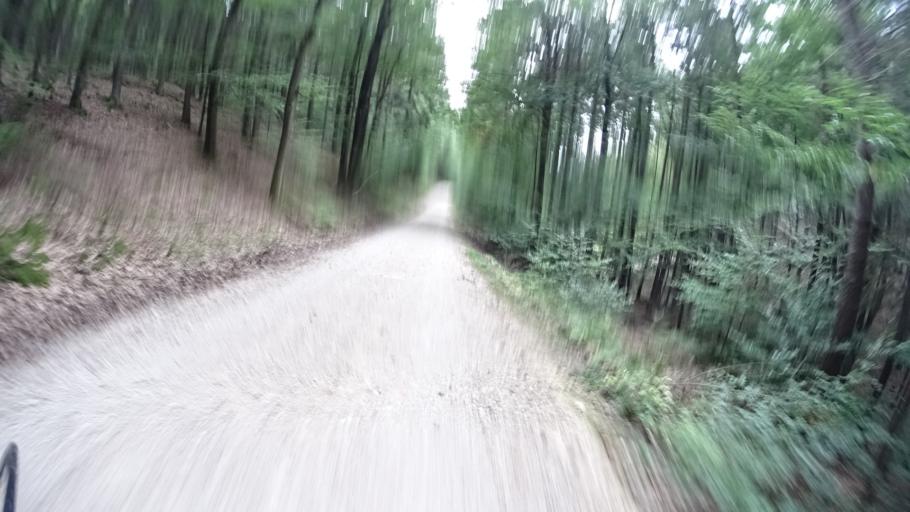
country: DE
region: Bavaria
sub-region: Upper Bavaria
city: Walting
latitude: 48.9146
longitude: 11.3188
